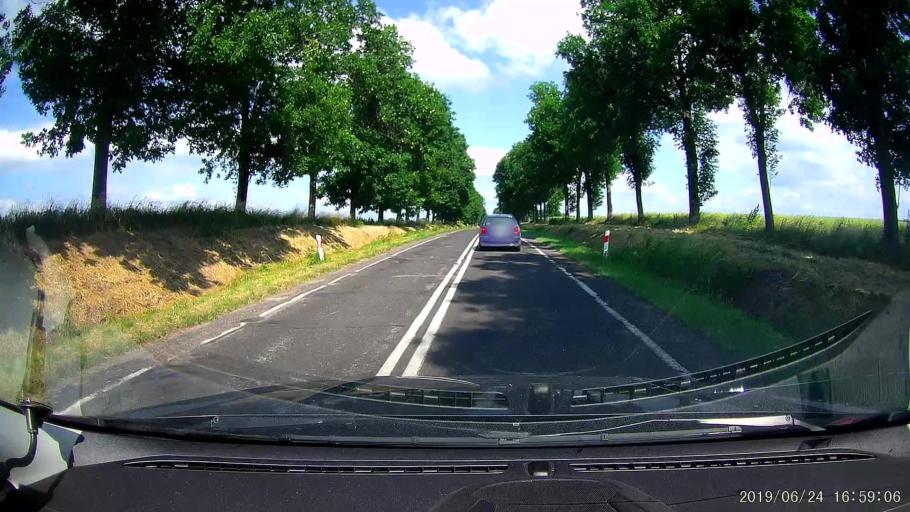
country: PL
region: Lublin Voivodeship
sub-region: Powiat tomaszowski
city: Telatyn
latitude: 50.5241
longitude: 23.8953
